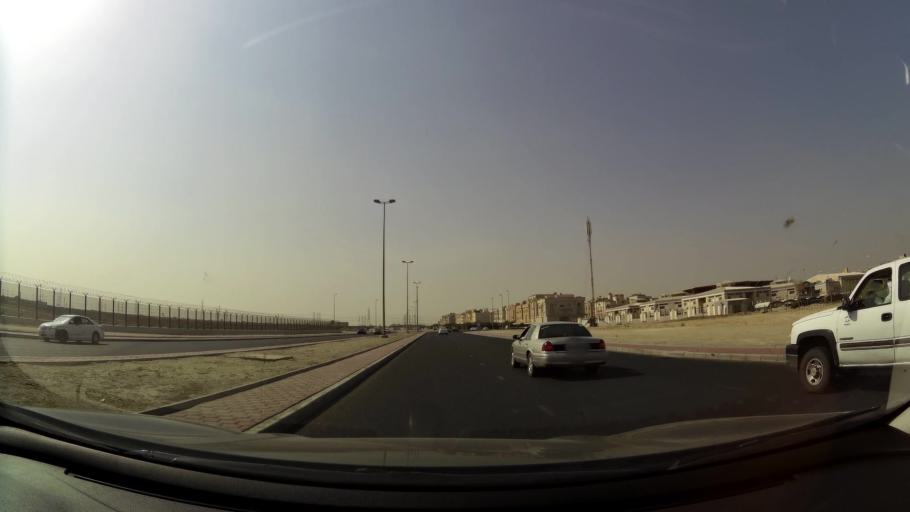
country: KW
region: Al Ahmadi
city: Ar Riqqah
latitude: 29.1222
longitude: 48.1013
